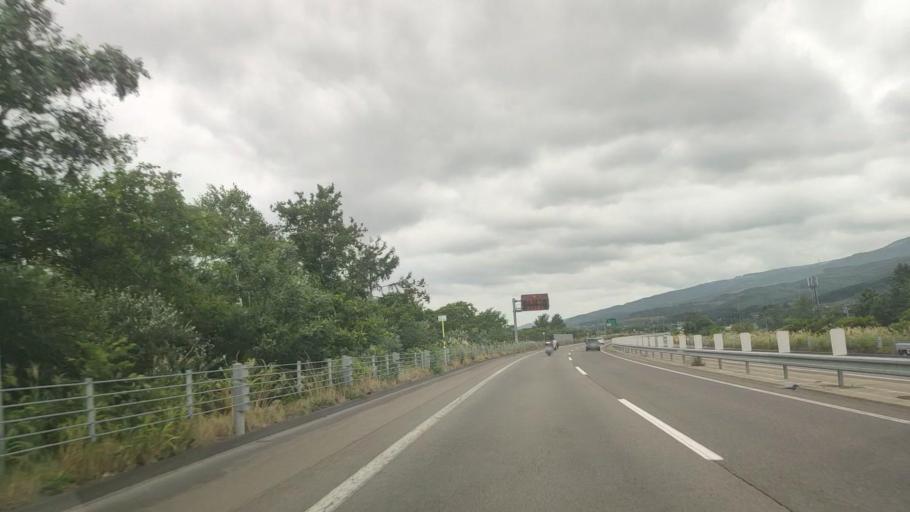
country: JP
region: Hokkaido
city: Nanae
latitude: 41.8624
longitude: 140.7319
